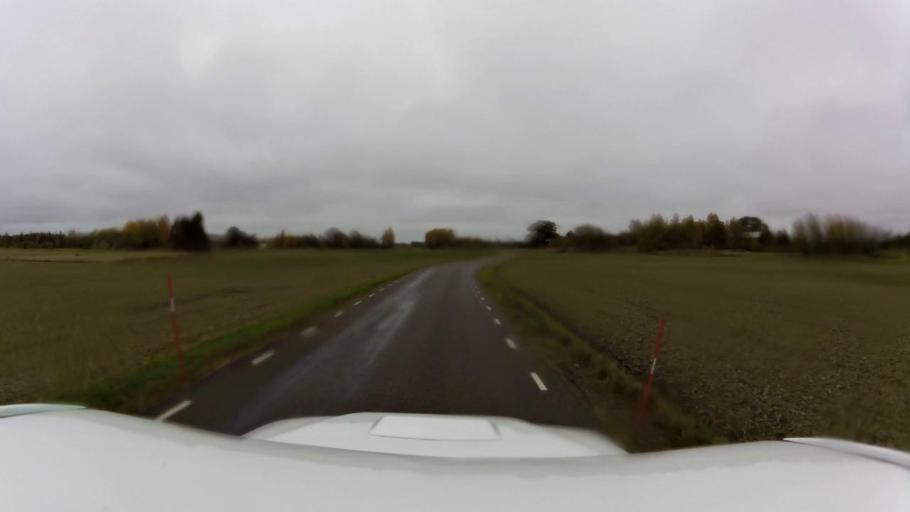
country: SE
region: OEstergoetland
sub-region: Linkopings Kommun
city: Linghem
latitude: 58.4737
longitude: 15.7222
